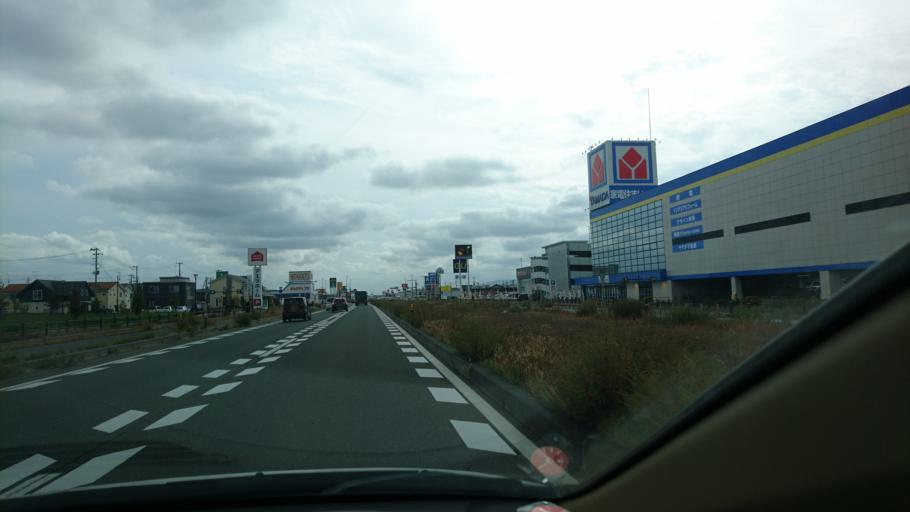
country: JP
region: Iwate
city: Morioka-shi
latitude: 39.6793
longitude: 141.1353
